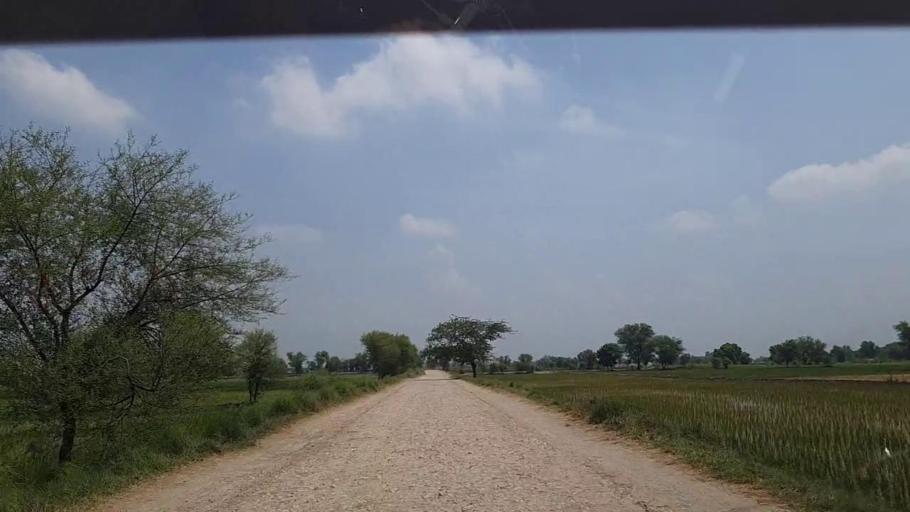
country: PK
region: Sindh
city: Khanpur
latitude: 27.8918
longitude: 69.4020
